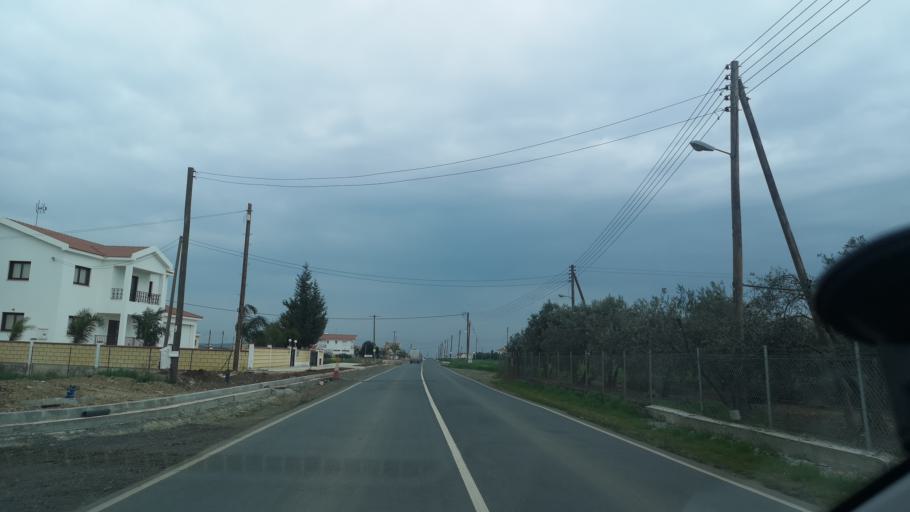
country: CY
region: Lefkosia
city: Tseri
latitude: 35.0774
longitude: 33.3107
